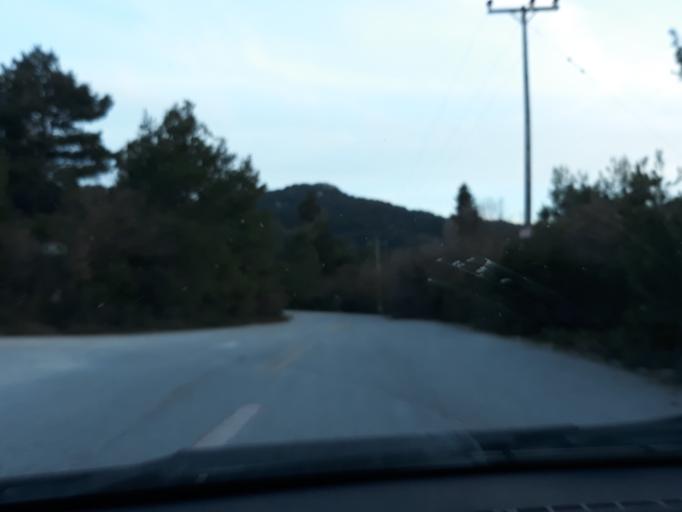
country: GR
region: Attica
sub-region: Nomarchia Anatolikis Attikis
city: Afidnes
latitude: 38.1931
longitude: 23.7944
